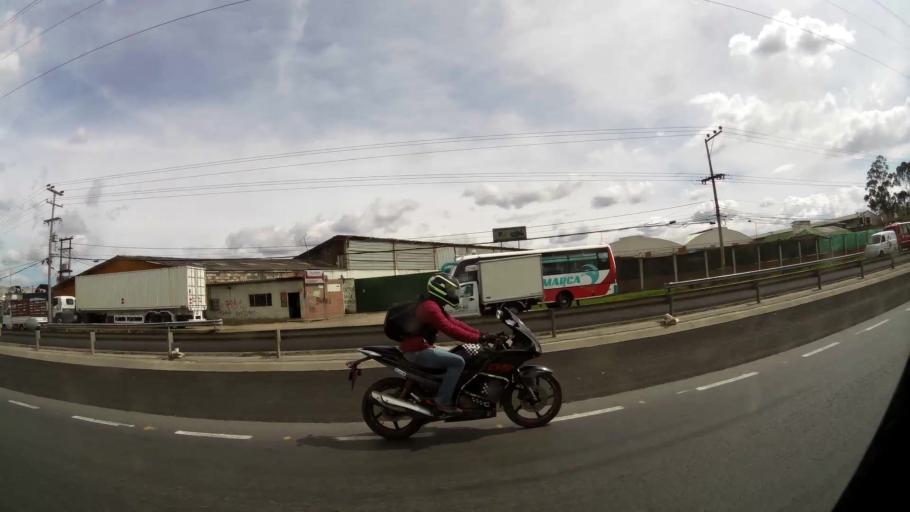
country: CO
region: Cundinamarca
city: Funza
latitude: 4.6993
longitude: -74.1836
